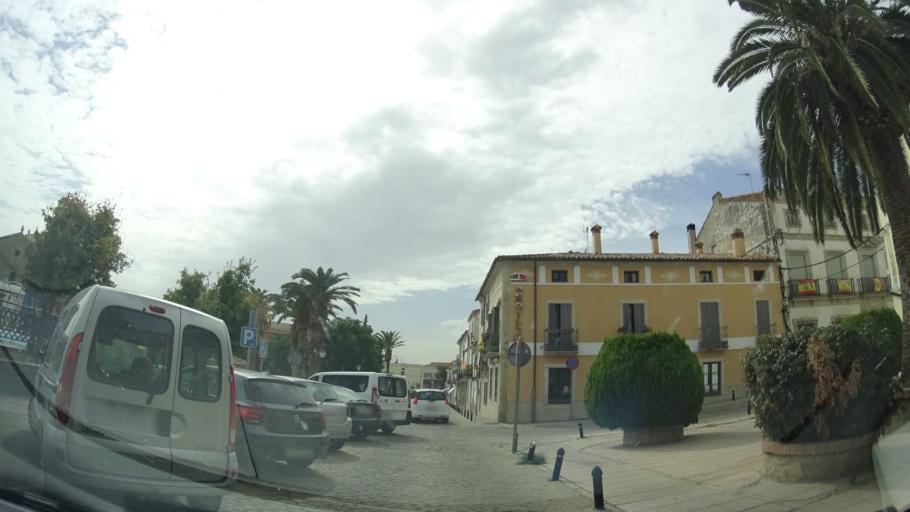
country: ES
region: Extremadura
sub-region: Provincia de Caceres
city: Trujillo
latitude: 39.4578
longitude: -5.8827
